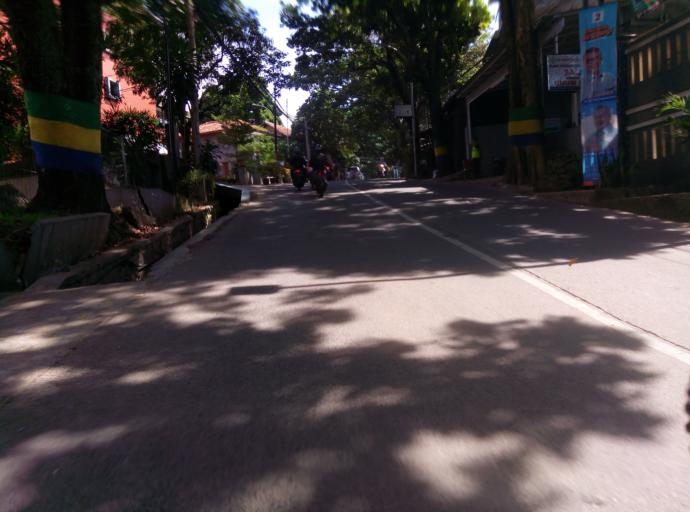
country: ID
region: West Java
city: Bandung
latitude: -6.8851
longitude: 107.6211
